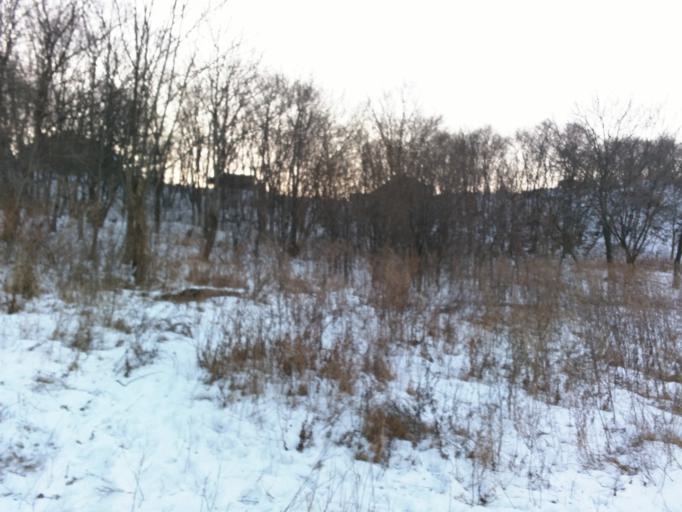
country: RU
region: Primorskiy
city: Vladivostok
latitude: 43.1793
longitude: 131.9277
